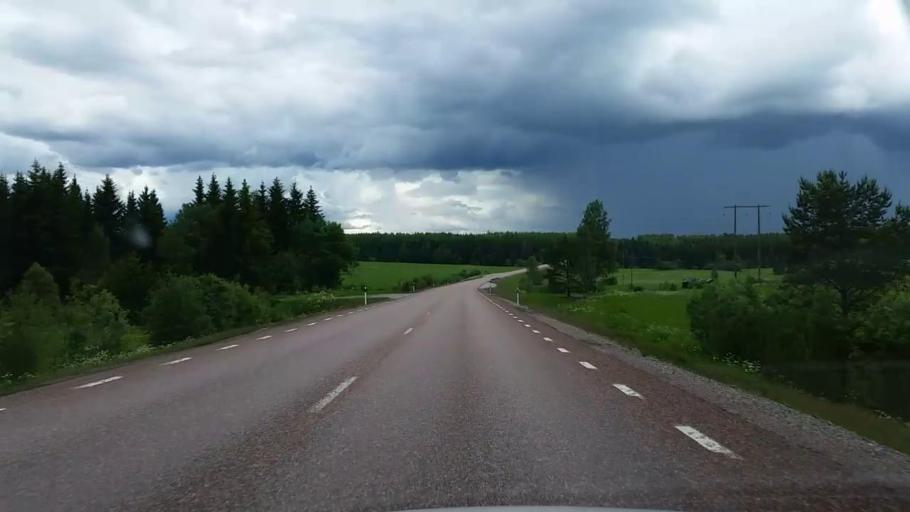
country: SE
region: Gaevleborg
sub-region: Hofors Kommun
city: Hofors
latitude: 60.5359
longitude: 16.4596
